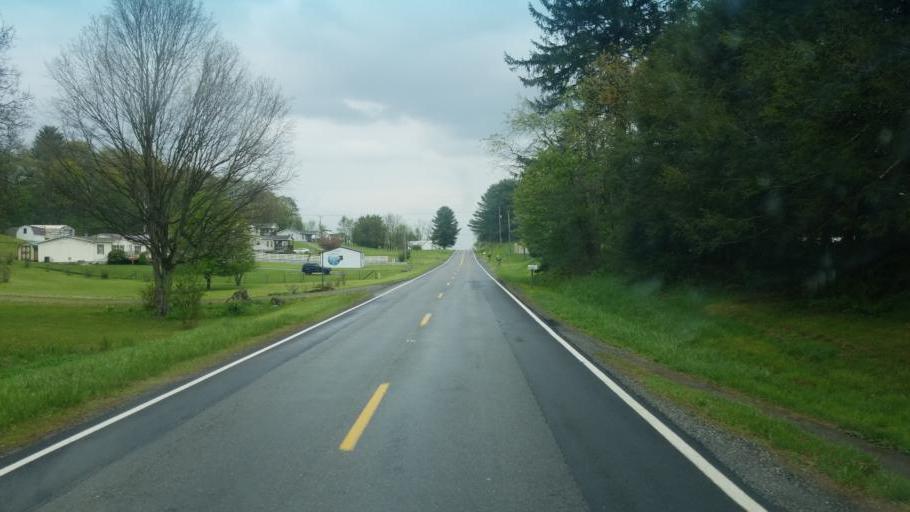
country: US
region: Virginia
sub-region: Wythe County
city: Rural Retreat
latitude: 36.9011
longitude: -81.3192
